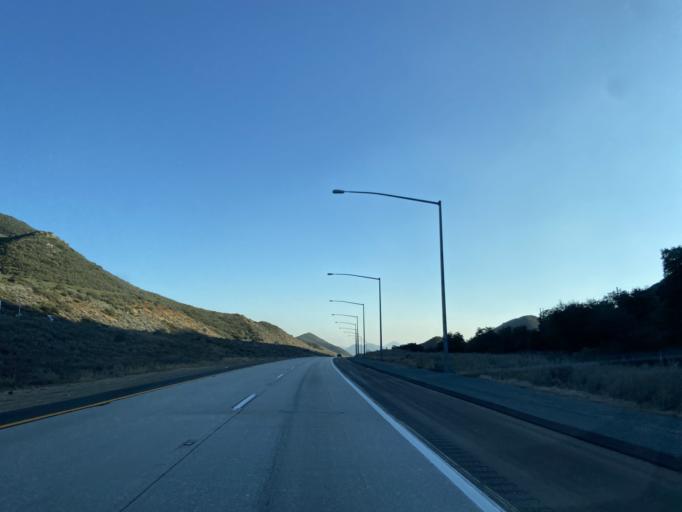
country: US
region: California
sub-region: San Diego County
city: Pine Valley
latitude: 32.7958
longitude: -116.4965
